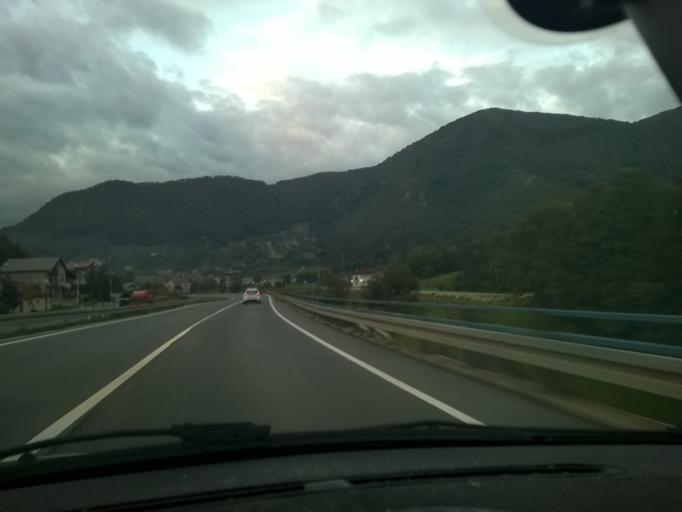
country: HR
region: Krapinsko-Zagorska
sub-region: Grad Krapina
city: Krapina
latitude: 46.1732
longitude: 15.8645
